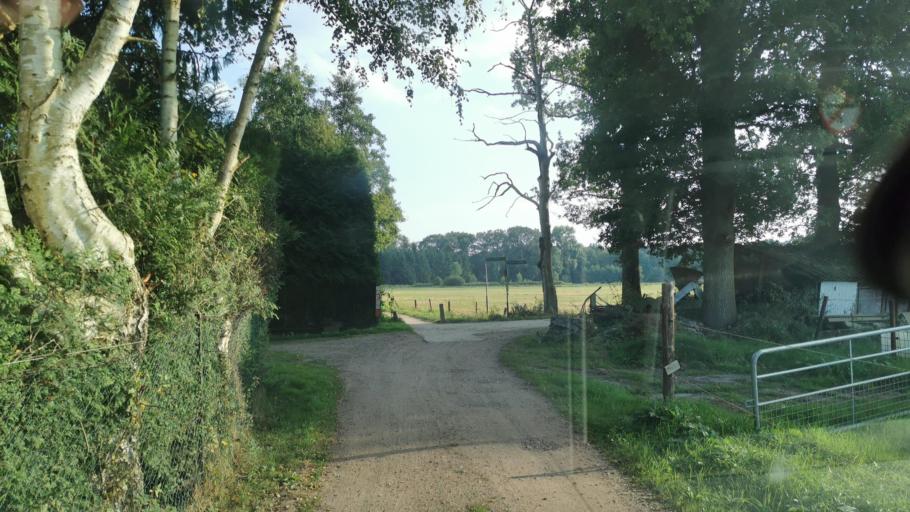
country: NL
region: Overijssel
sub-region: Gemeente Losser
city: Losser
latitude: 52.2903
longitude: 6.9765
